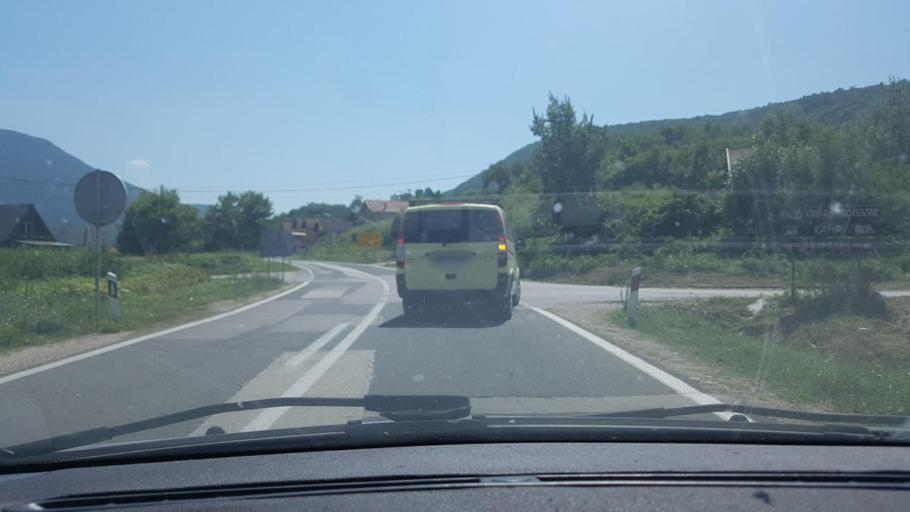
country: BA
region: Federation of Bosnia and Herzegovina
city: Bihac
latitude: 44.7699
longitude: 15.9443
